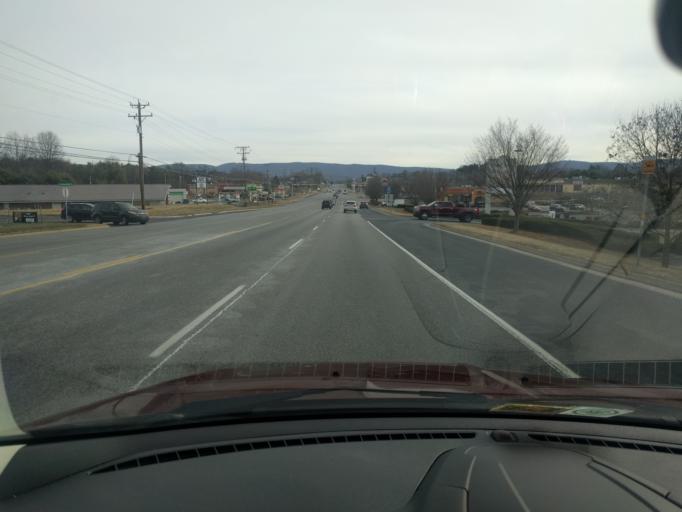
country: US
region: Virginia
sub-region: Augusta County
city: Fishersville
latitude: 38.0833
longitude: -78.9318
